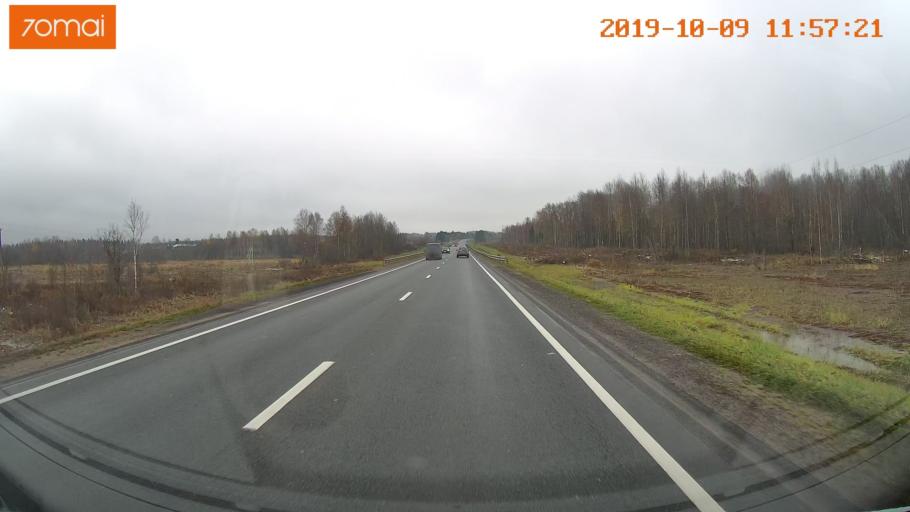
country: RU
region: Vologda
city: Gryazovets
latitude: 58.7334
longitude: 40.2921
